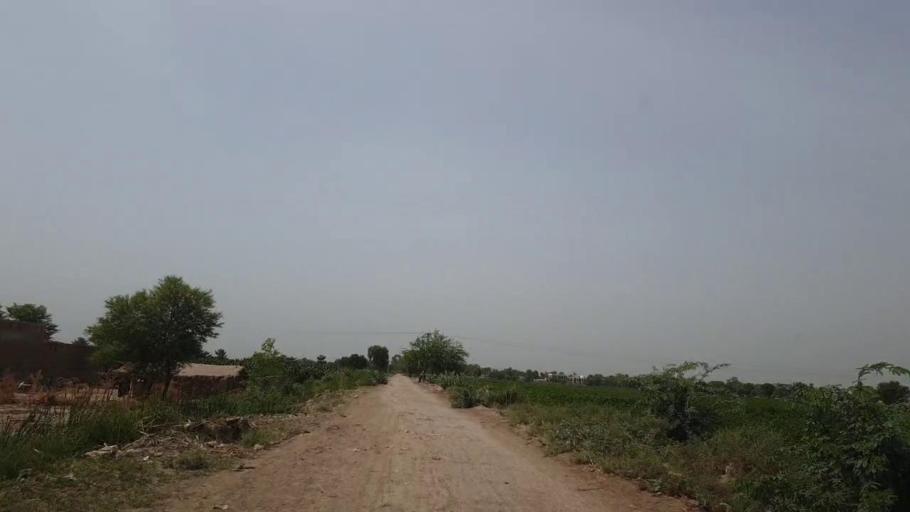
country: PK
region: Sindh
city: Sakrand
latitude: 26.1330
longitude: 68.2865
